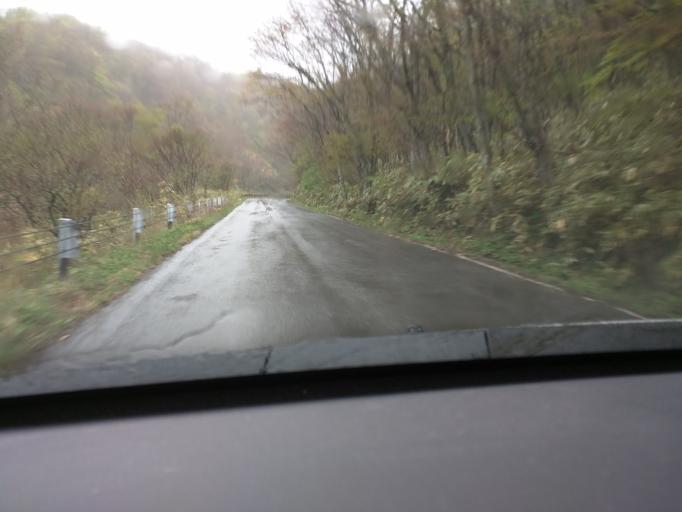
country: JP
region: Fukushima
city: Inawashiro
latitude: 37.6616
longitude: 140.2575
